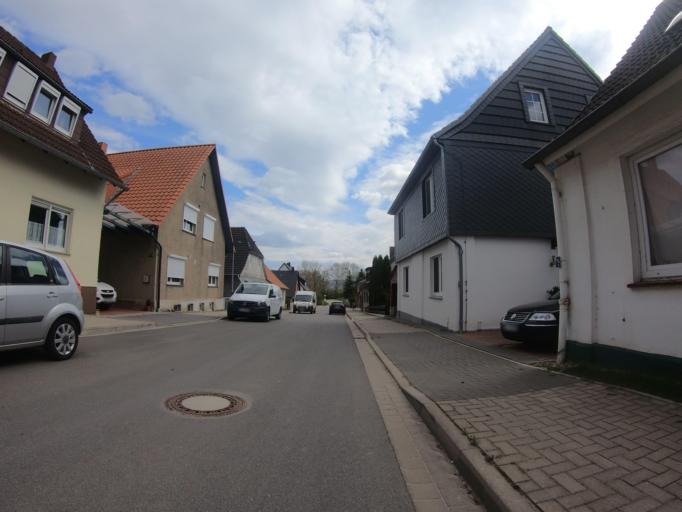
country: DE
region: Lower Saxony
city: Nordstemmen
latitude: 52.1907
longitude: 9.7788
